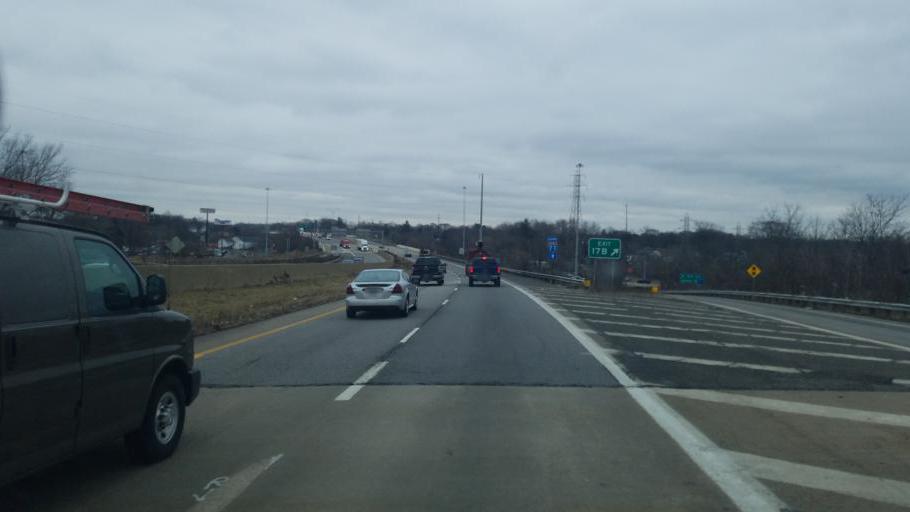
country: US
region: Ohio
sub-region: Summit County
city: Barberton
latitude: 41.0363
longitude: -81.5819
